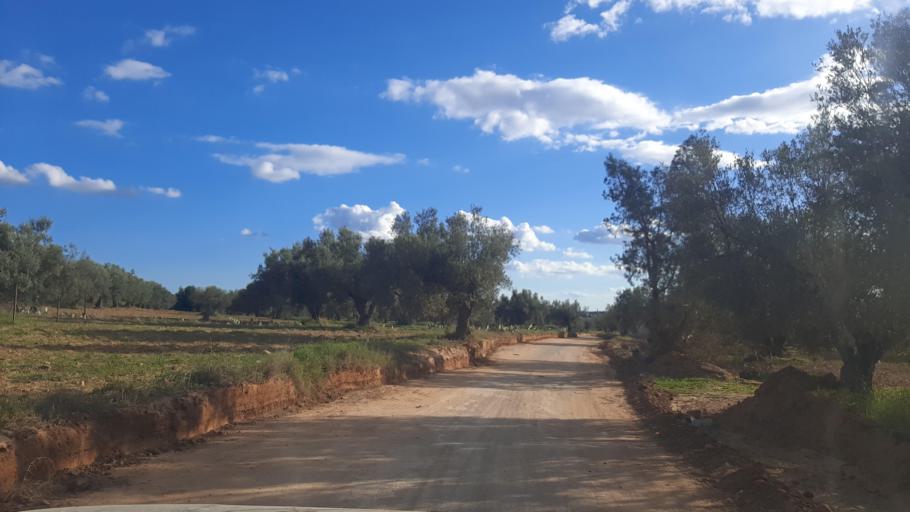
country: TN
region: Nabul
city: Al Hammamat
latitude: 36.4258
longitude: 10.5078
